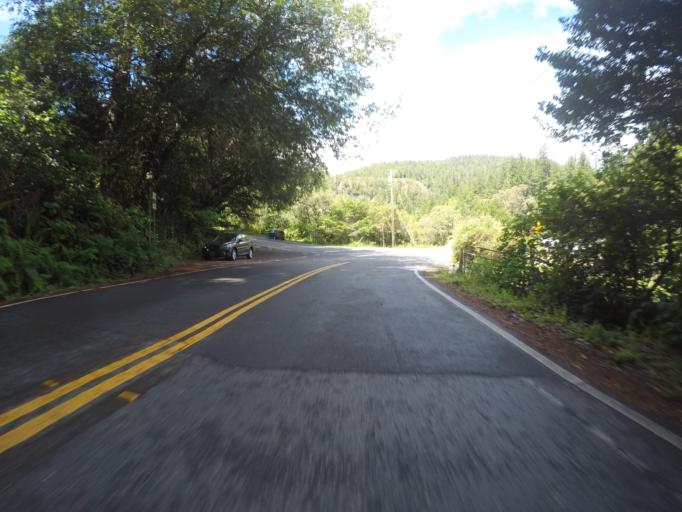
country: US
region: California
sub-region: Del Norte County
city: Bertsch-Oceanview
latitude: 41.7968
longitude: -124.0538
